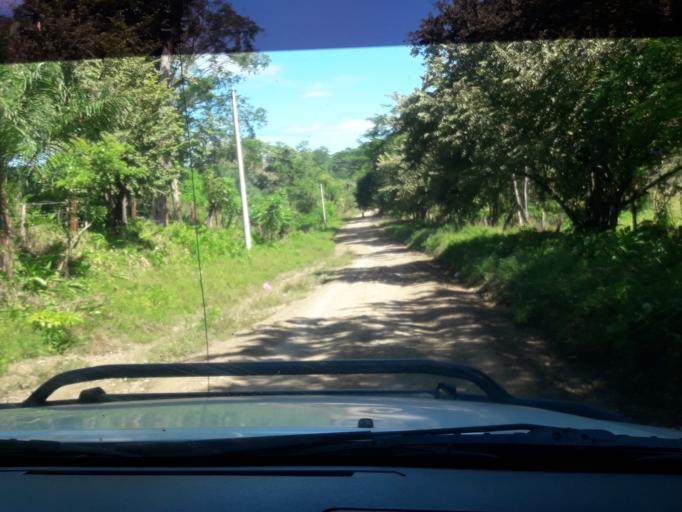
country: NI
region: Rivas
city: Cardenas
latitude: 11.2223
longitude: -85.6491
